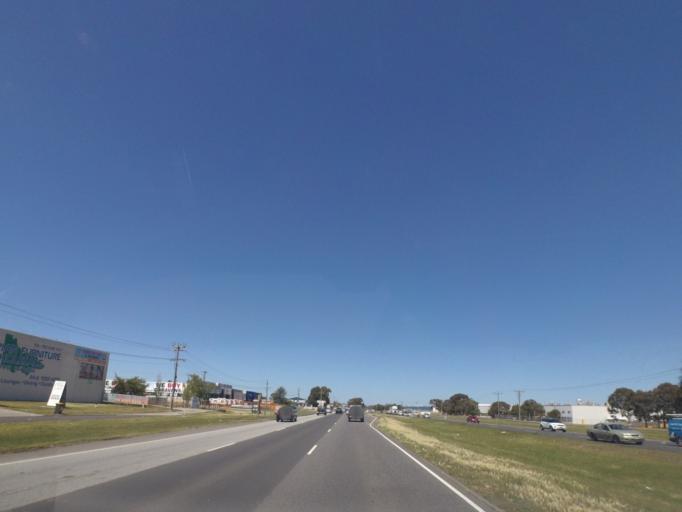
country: AU
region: Victoria
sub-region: Hume
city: Coolaroo
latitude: -37.6573
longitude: 144.9536
